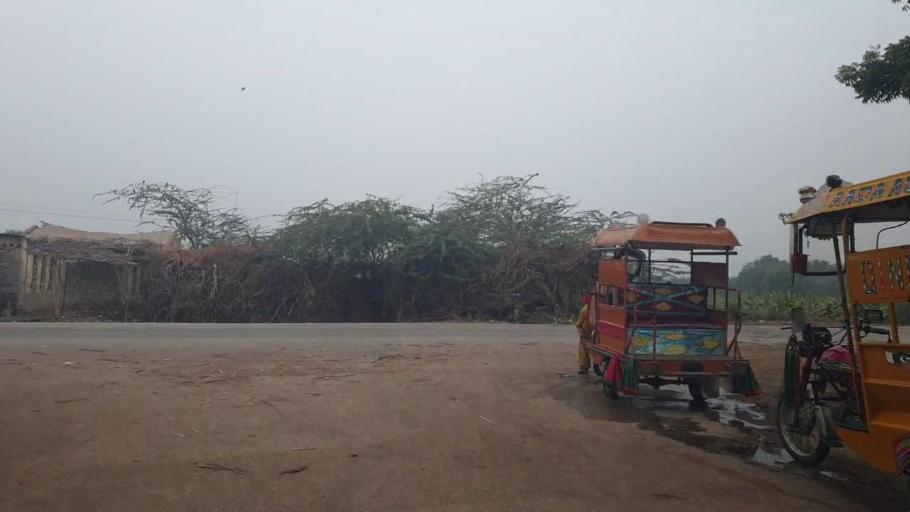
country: PK
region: Sindh
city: Tando Adam
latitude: 25.7307
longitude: 68.6685
